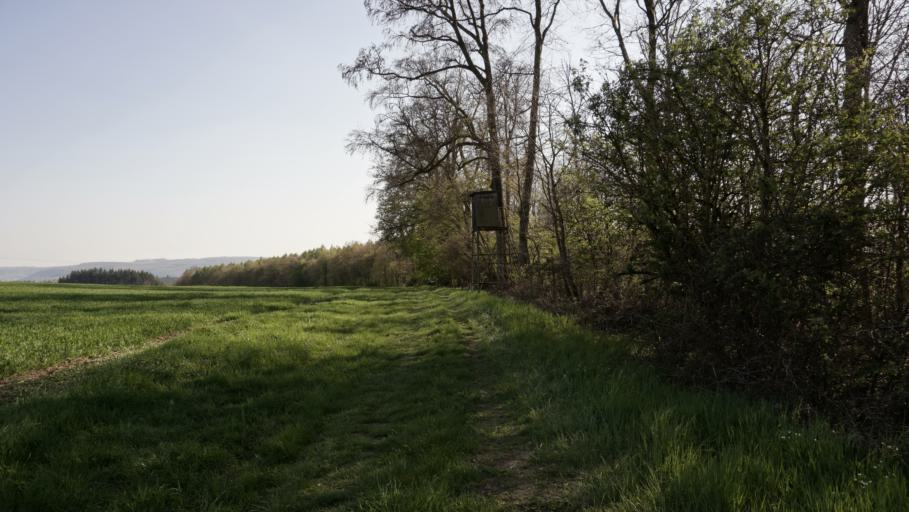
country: DE
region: Baden-Wuerttemberg
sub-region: Karlsruhe Region
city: Neckargerach
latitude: 49.3986
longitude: 9.0848
